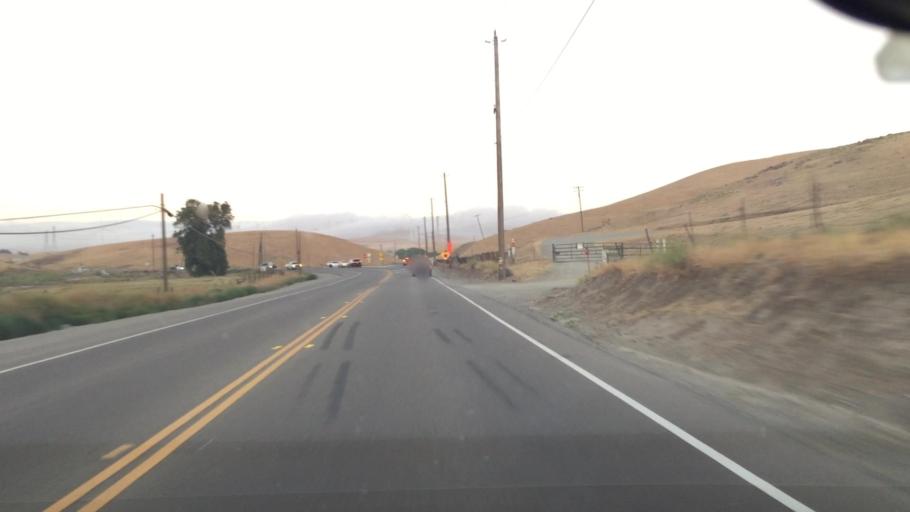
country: US
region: California
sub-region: San Joaquin County
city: Mountain House
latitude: 37.7473
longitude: -121.5824
